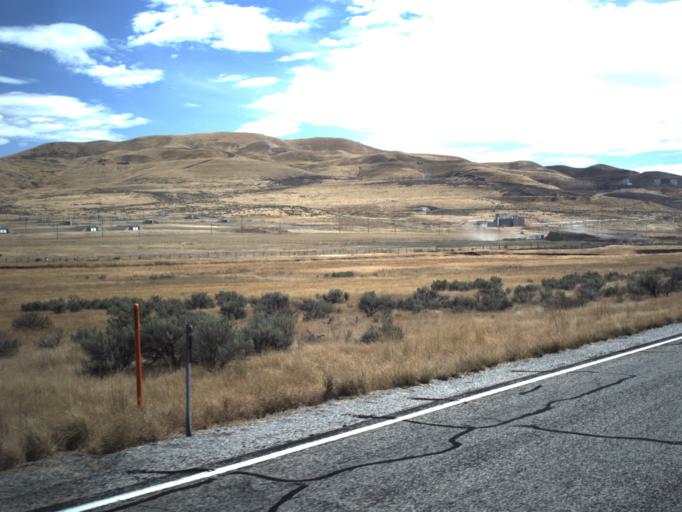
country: US
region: Utah
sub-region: Box Elder County
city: Tremonton
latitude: 41.7005
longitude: -112.4474
